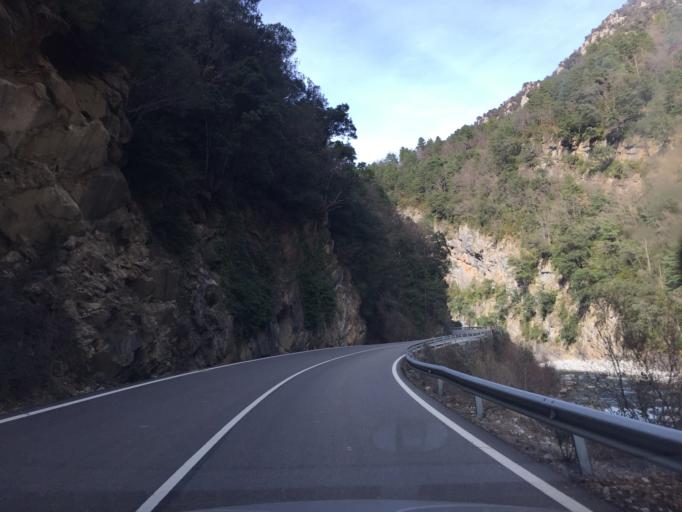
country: ES
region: Aragon
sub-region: Provincia de Huesca
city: Bielsa
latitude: 42.5674
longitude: 0.2052
